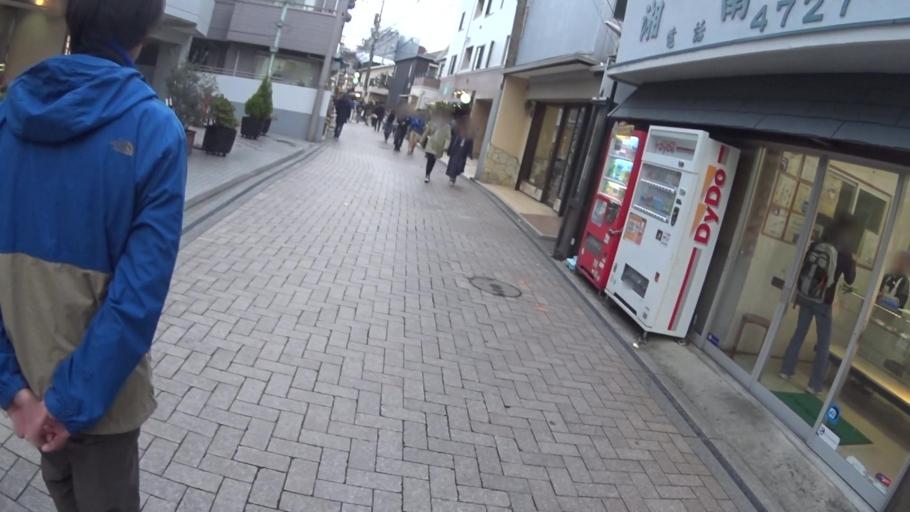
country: JP
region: Kanagawa
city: Fujisawa
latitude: 35.3096
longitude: 139.4870
